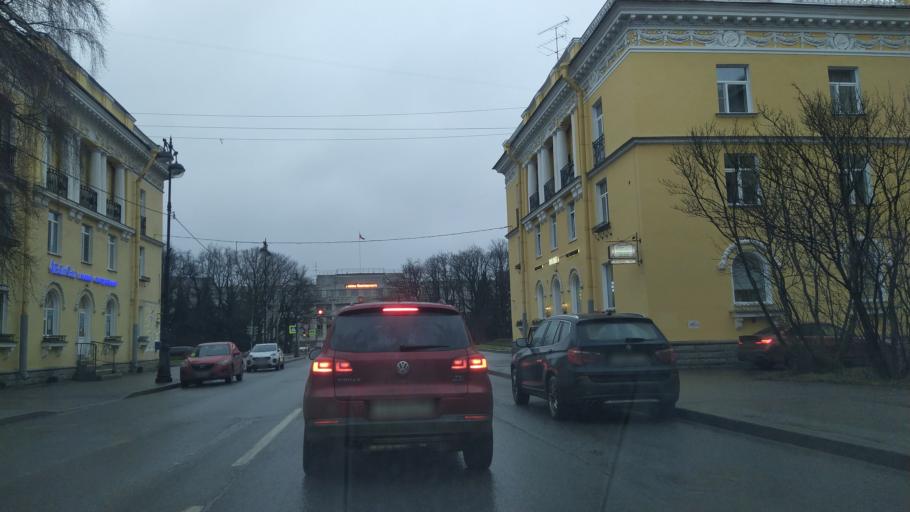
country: RU
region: St.-Petersburg
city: Pushkin
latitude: 59.7212
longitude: 30.4152
